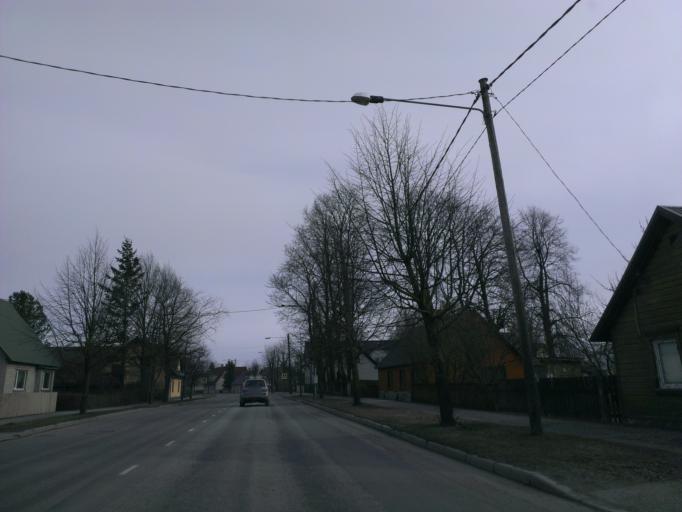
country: EE
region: Paernumaa
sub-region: Paernu linn
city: Parnu
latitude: 58.3910
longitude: 24.4661
